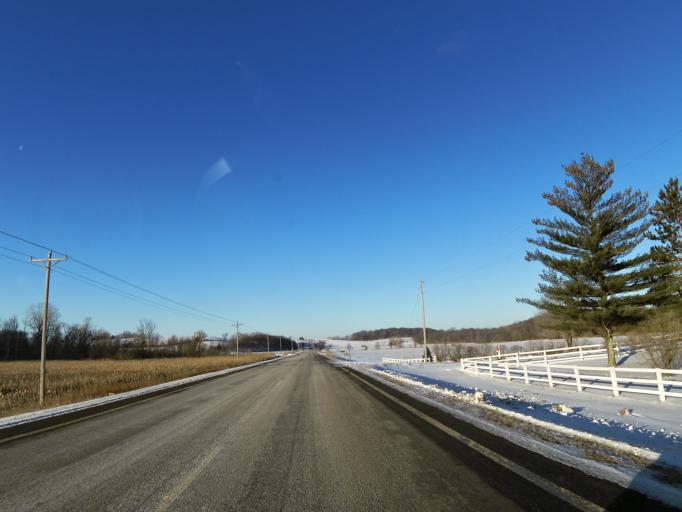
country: US
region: Minnesota
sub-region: Le Sueur County
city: New Prague
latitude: 44.6307
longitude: -93.5370
